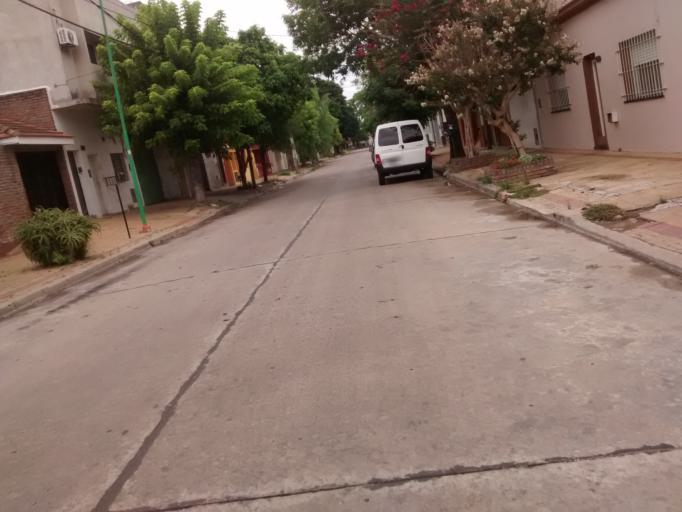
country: AR
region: Buenos Aires
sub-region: Partido de La Plata
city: La Plata
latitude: -34.8969
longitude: -57.9688
